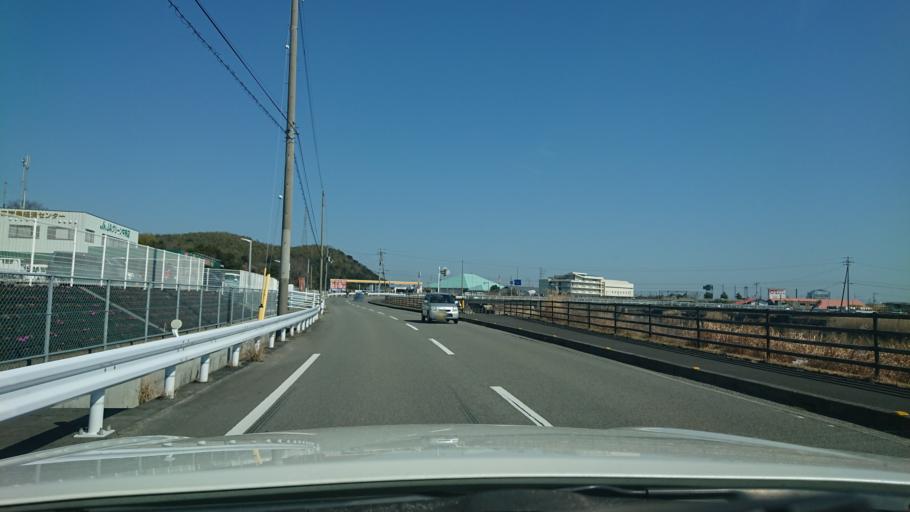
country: JP
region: Tokushima
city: Komatsushimacho
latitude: 33.9753
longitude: 134.6031
